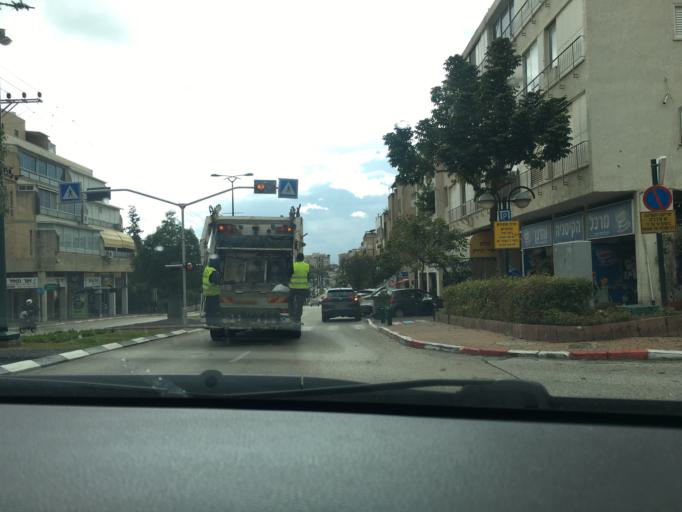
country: IL
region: Tel Aviv
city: Ramat HaSharon
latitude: 32.1413
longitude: 34.8428
